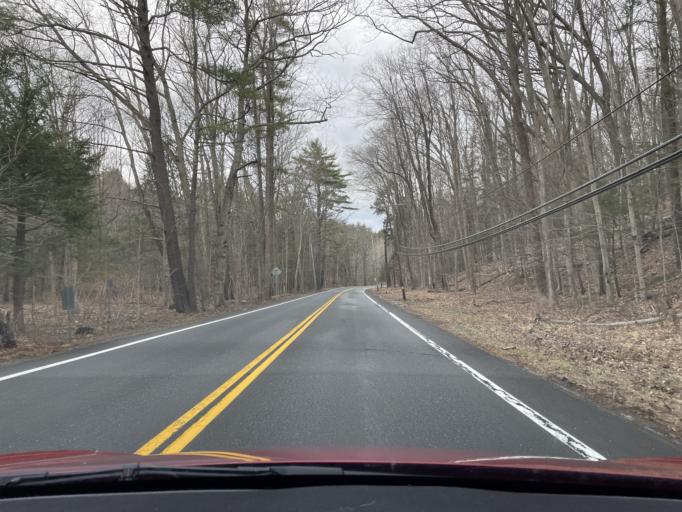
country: US
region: New York
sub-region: Ulster County
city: Woodstock
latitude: 42.0503
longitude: -74.1595
